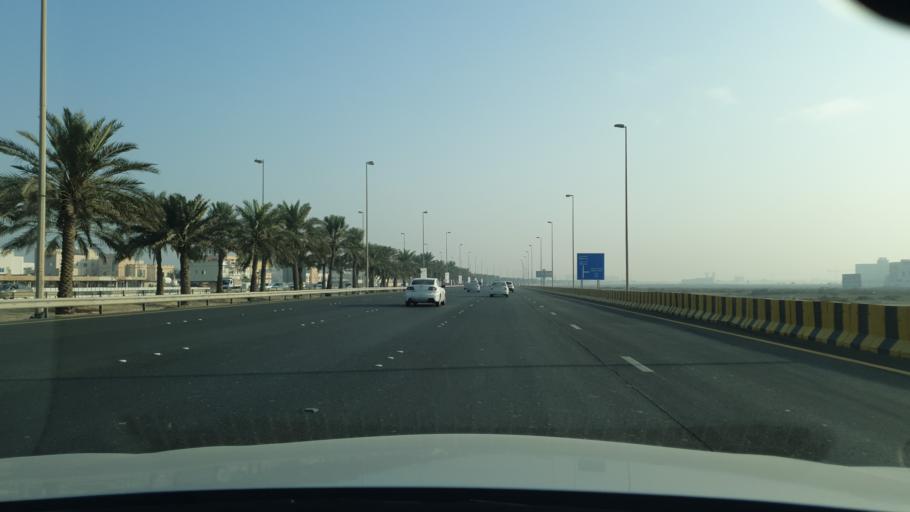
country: BH
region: Northern
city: Madinat `Isa
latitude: 26.1884
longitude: 50.5099
